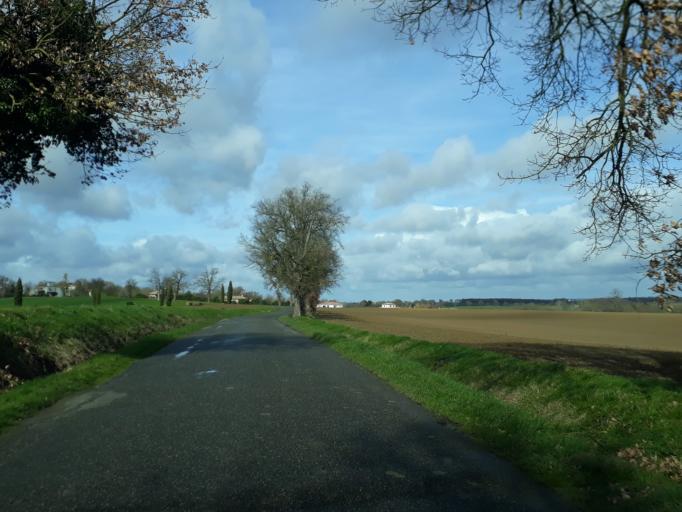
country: FR
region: Midi-Pyrenees
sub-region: Departement du Gers
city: Gimont
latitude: 43.6358
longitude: 1.0057
